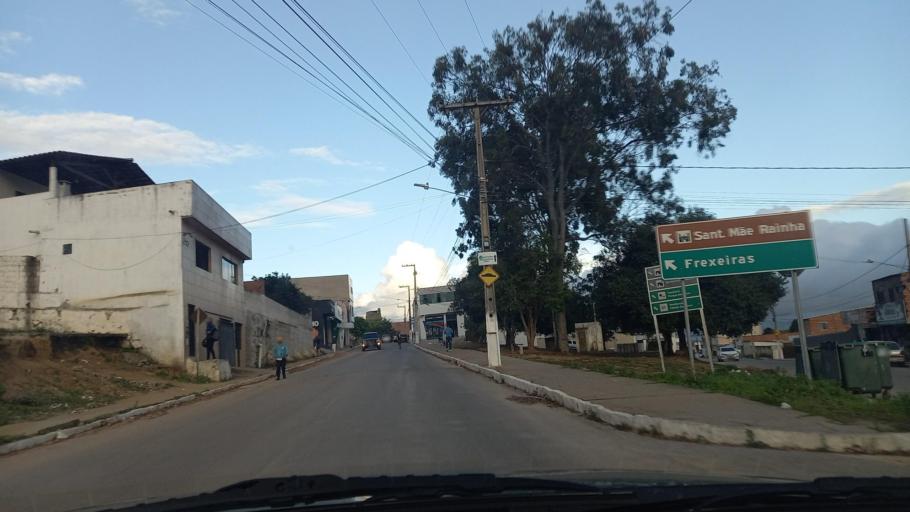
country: BR
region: Pernambuco
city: Garanhuns
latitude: -8.8878
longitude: -36.4618
